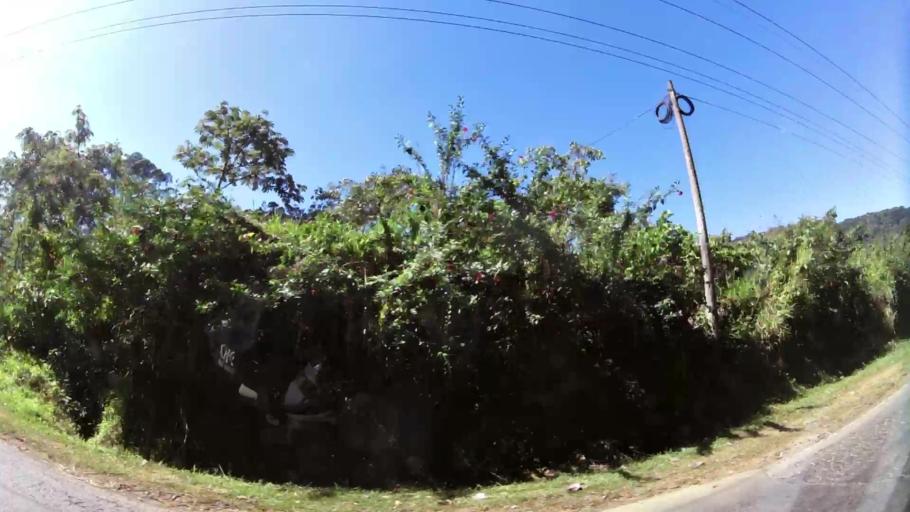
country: SV
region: Ahuachapan
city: Concepcion de Ataco
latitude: 13.8818
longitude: -89.8425
